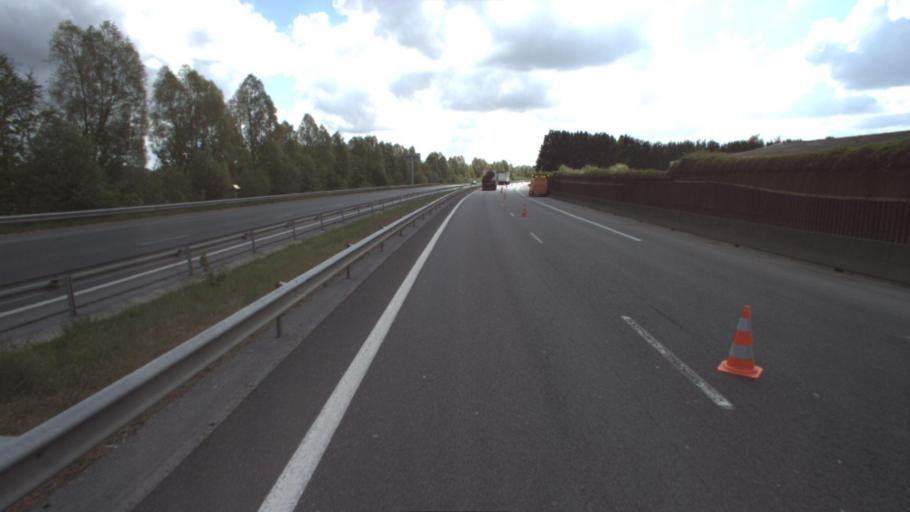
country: FR
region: Ile-de-France
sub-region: Departement de Seine-et-Marne
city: Fontenay-Tresigny
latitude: 48.7112
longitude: 2.8750
